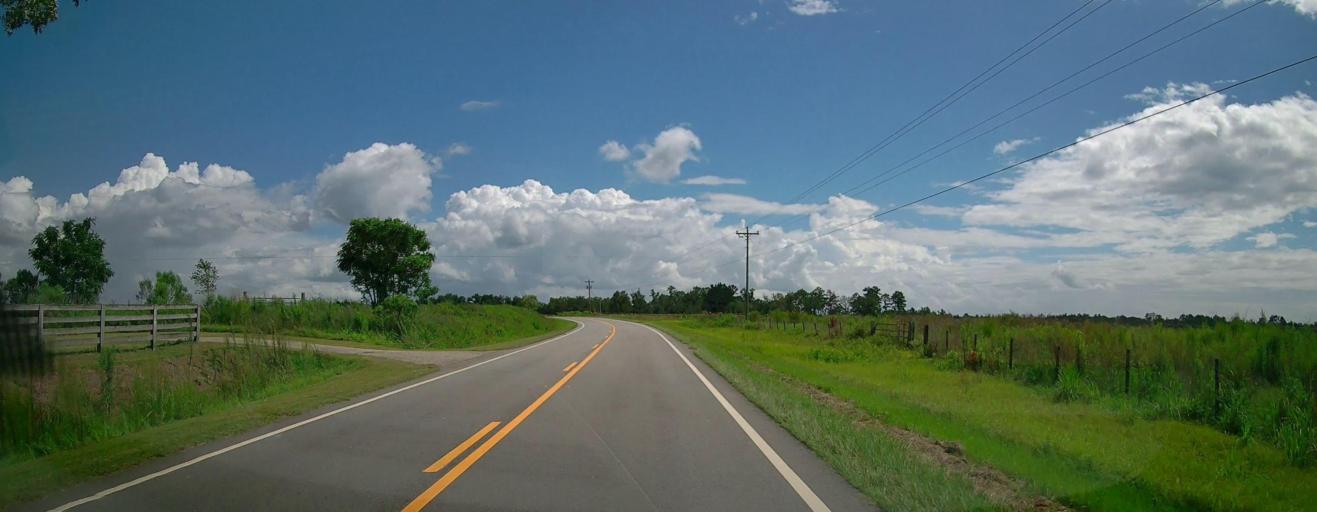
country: US
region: Georgia
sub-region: Irwin County
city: Ocilla
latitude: 31.6061
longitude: -83.1660
